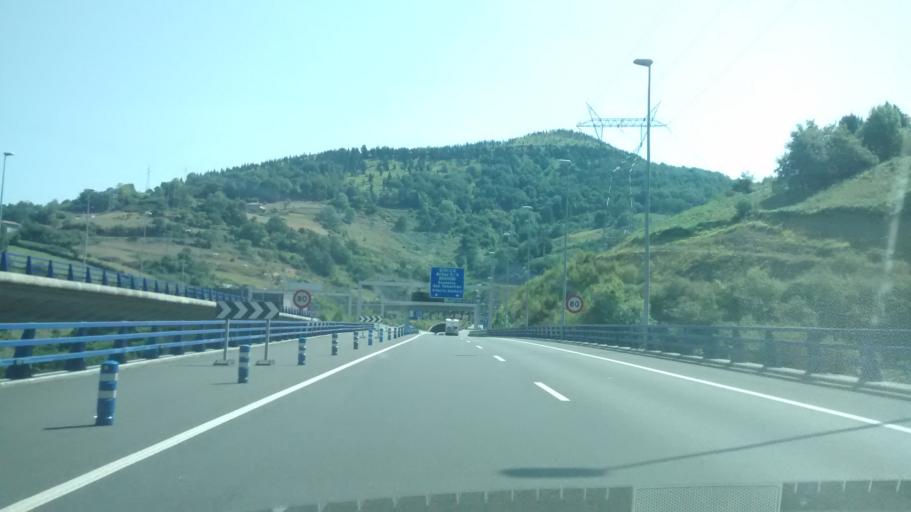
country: ES
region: Basque Country
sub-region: Bizkaia
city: Bilbao
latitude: 43.2378
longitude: -2.9499
